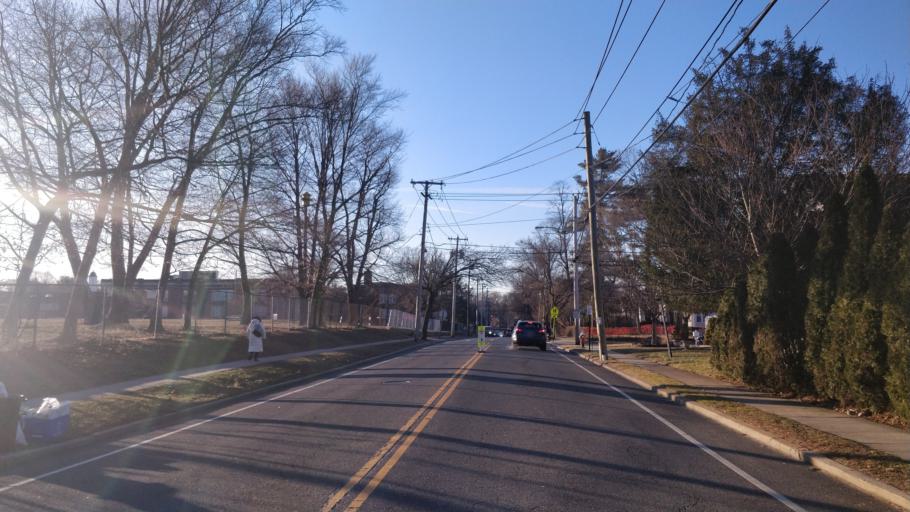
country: US
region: New York
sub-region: Nassau County
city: Glen Cove
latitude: 40.8729
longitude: -73.6305
